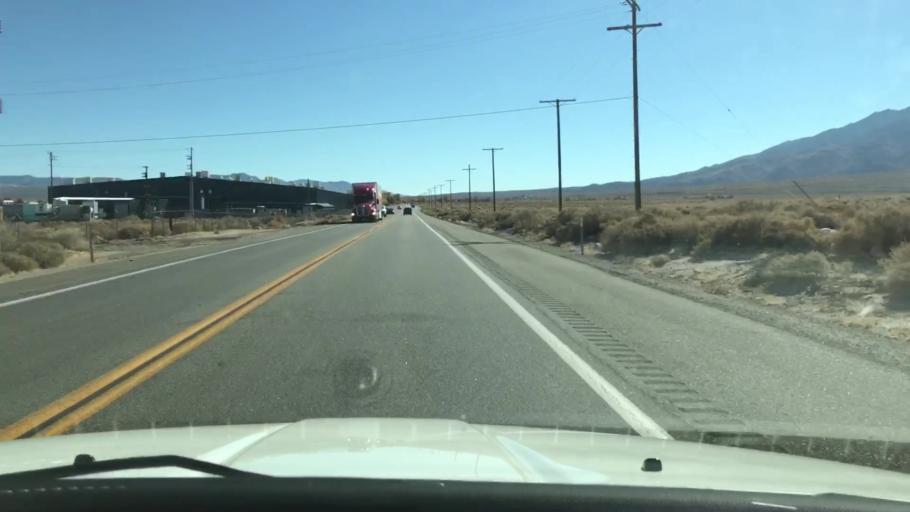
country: US
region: California
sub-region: Inyo County
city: Lone Pine
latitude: 36.3081
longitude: -118.0243
